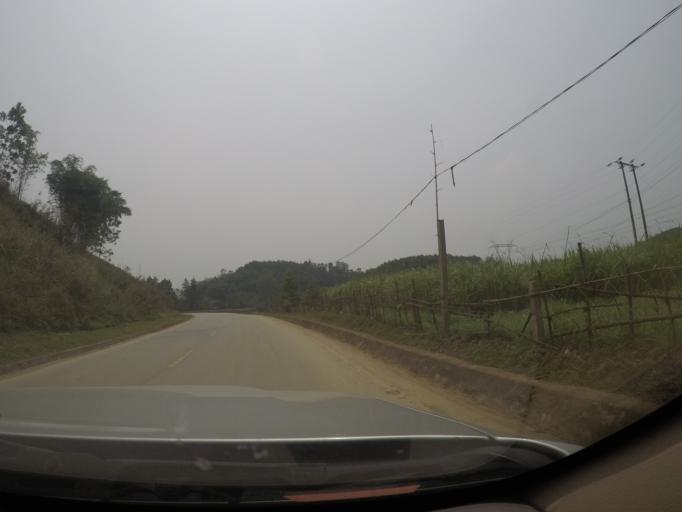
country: VN
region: Thanh Hoa
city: Thi Tran Thuong Xuan
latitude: 19.8293
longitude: 105.3891
